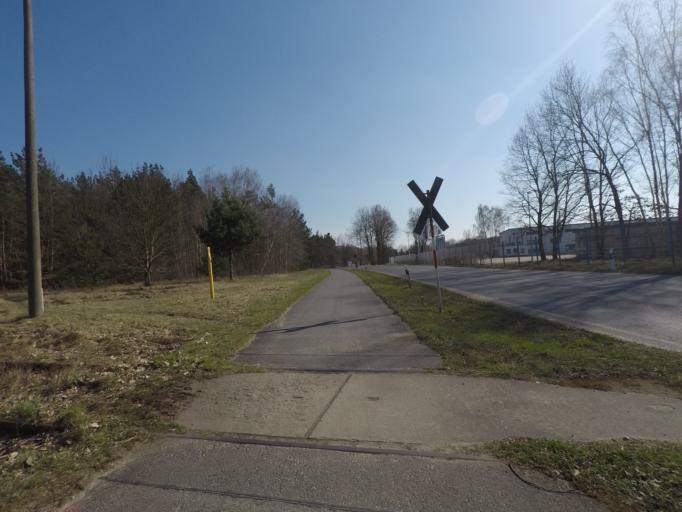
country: DE
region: Brandenburg
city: Eberswalde
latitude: 52.8502
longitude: 13.7740
